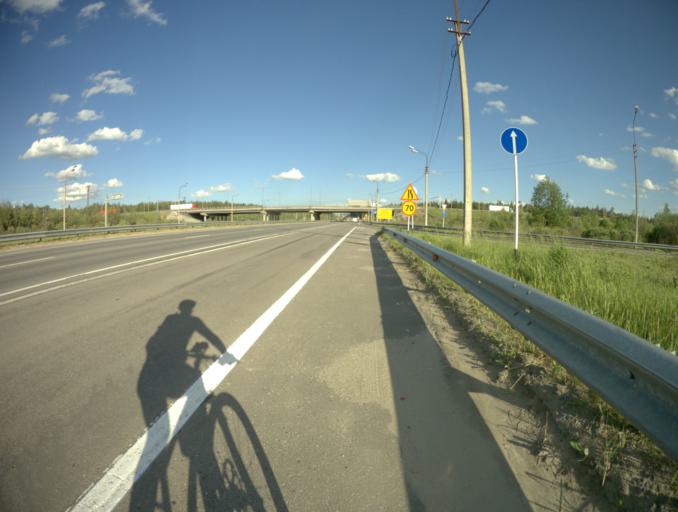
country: RU
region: Vladimir
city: Kommunar
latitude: 56.0805
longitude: 40.4711
